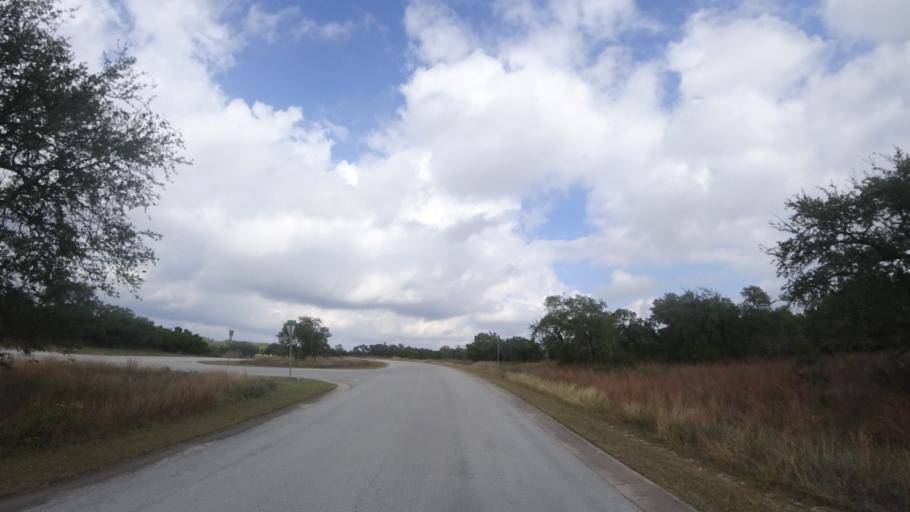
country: US
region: Texas
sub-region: Travis County
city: Barton Creek
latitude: 30.3014
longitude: -97.8911
